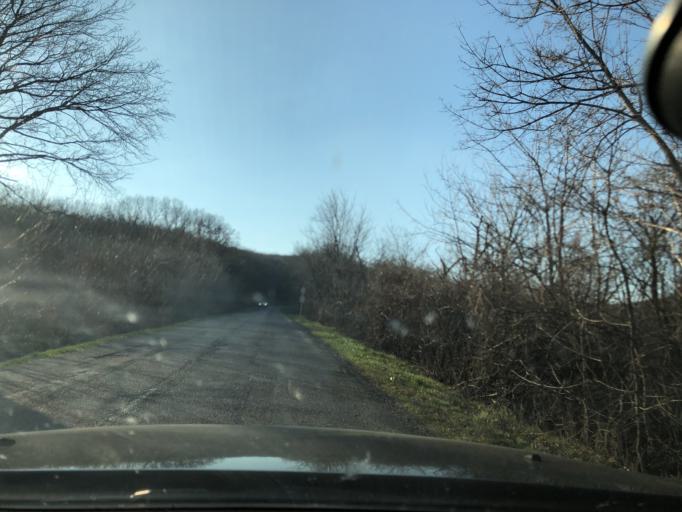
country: HU
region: Nograd
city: Paszto
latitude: 47.9146
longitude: 19.6429
